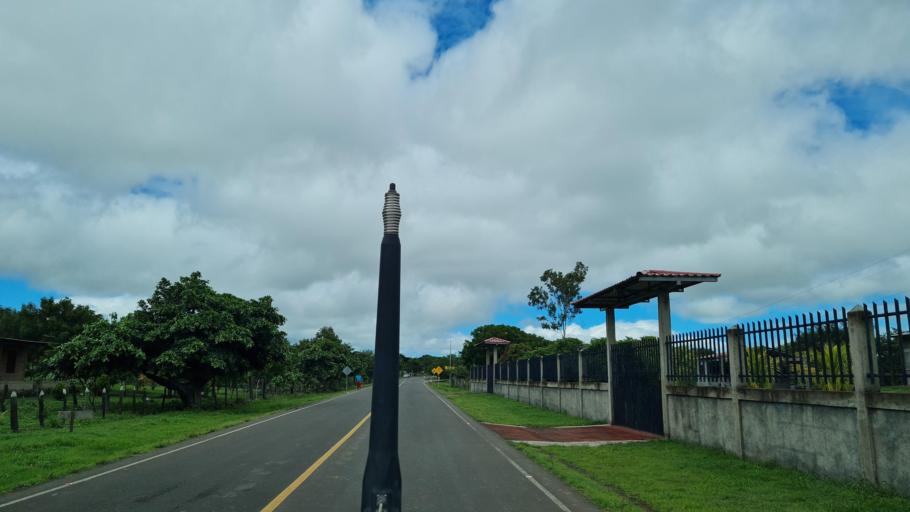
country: NI
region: Matagalpa
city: Terrabona
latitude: 12.5918
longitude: -85.9580
